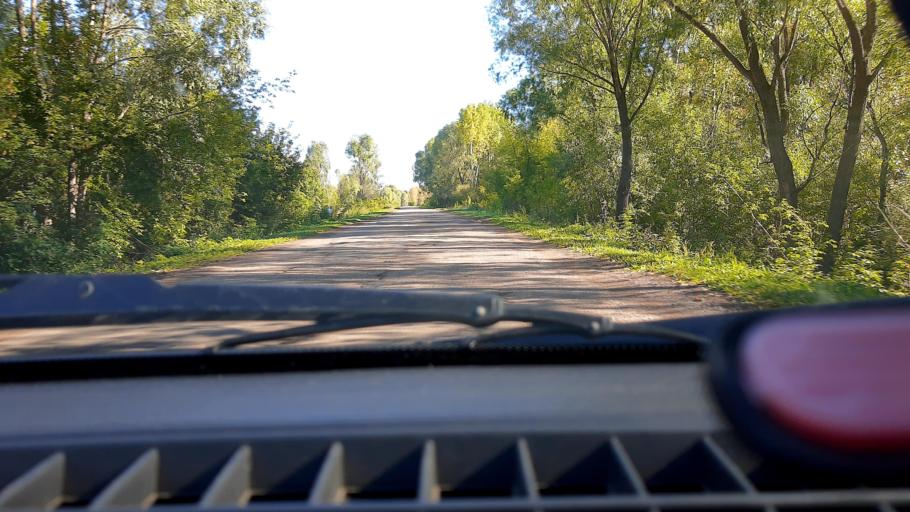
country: RU
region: Bashkortostan
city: Kushnarenkovo
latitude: 55.1005
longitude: 55.5109
